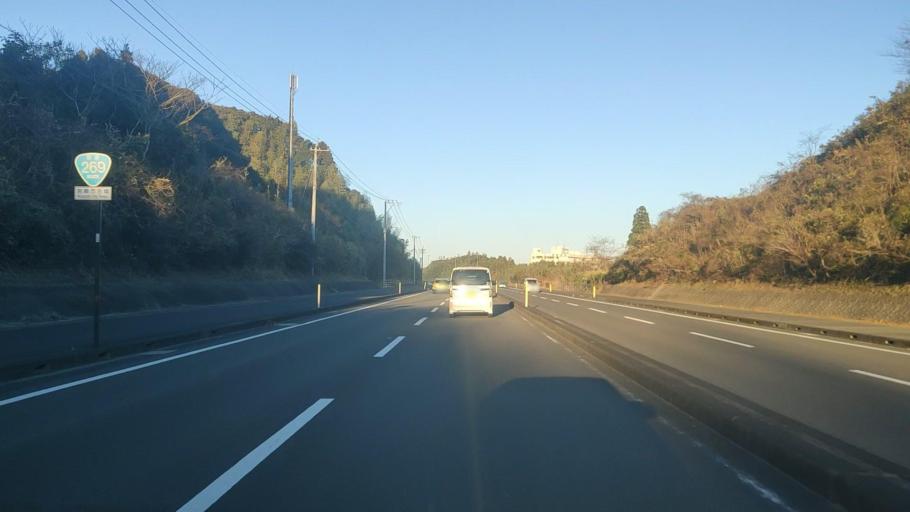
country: JP
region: Miyazaki
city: Miyazaki-shi
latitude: 31.8850
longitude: 131.3996
